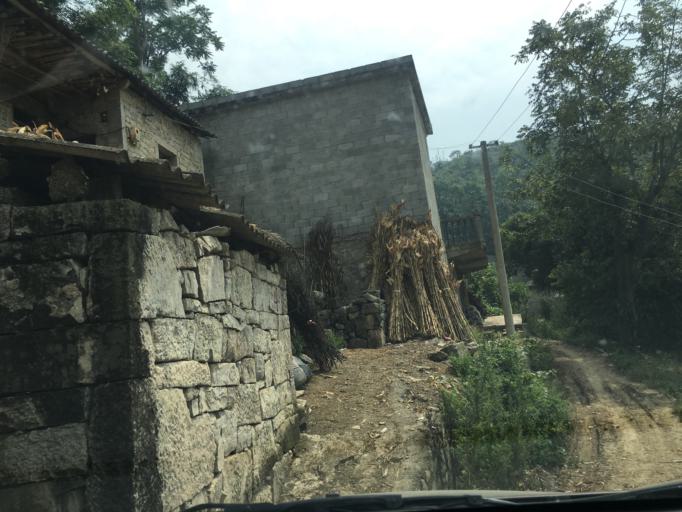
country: CN
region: Guizhou Sheng
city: Anshun
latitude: 25.5973
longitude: 105.6745
